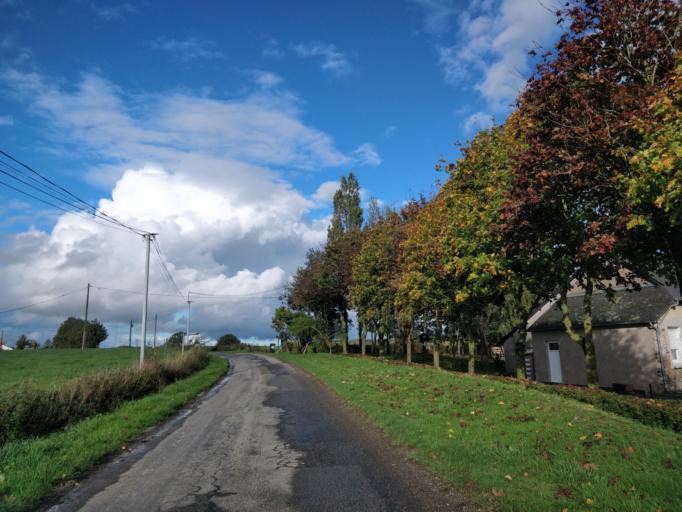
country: FR
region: Brittany
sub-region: Departement d'Ille-et-Vilaine
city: Chateaubourg
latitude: 48.1224
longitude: -1.4265
